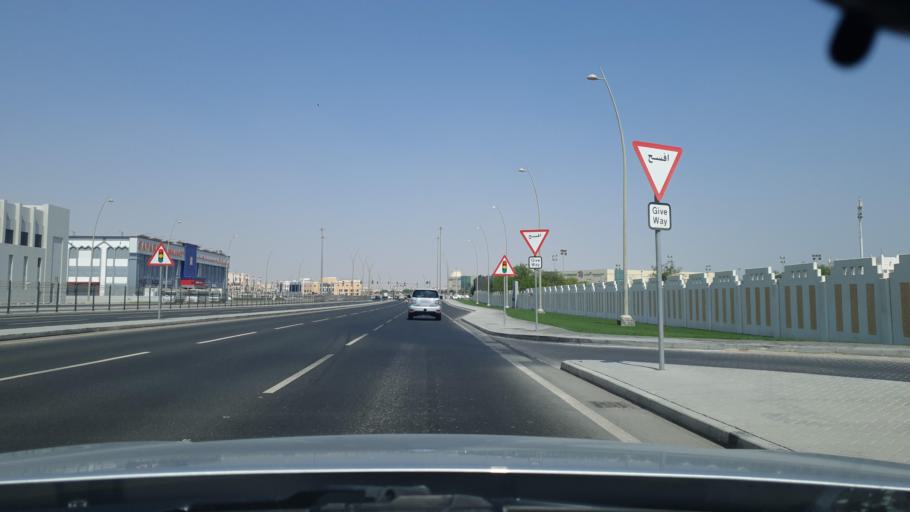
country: QA
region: Al Khawr
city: Al Khawr
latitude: 25.6709
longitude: 51.5011
